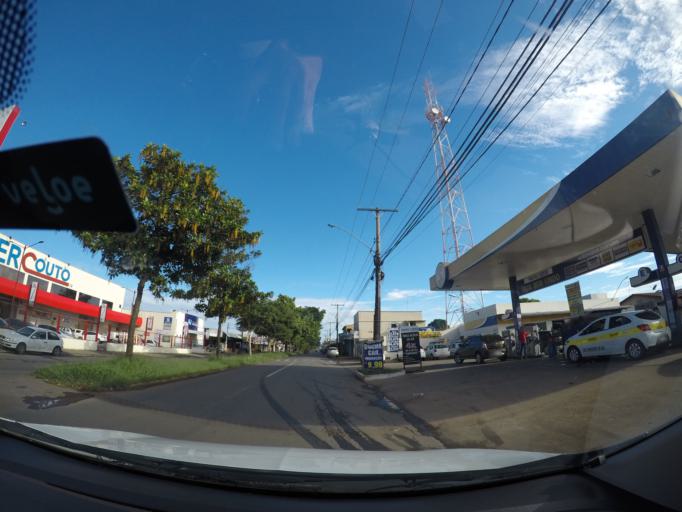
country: BR
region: Goias
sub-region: Aparecida De Goiania
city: Aparecida de Goiania
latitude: -16.7535
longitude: -49.2791
